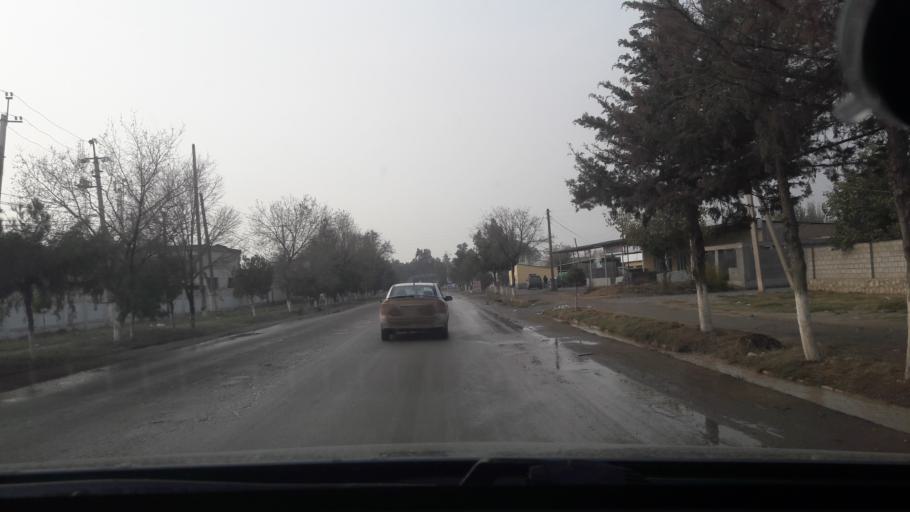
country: TJ
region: Khatlon
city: Abdurahmoni Jomi
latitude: 37.9823
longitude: 68.6972
